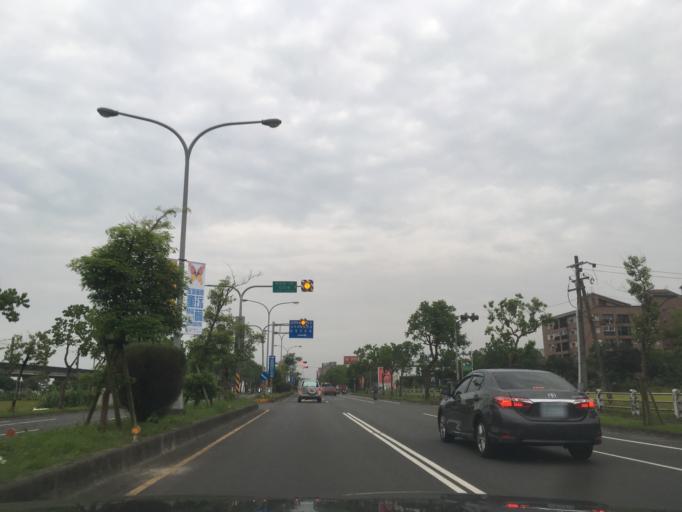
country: TW
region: Taiwan
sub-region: Yilan
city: Yilan
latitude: 24.7356
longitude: 121.7623
